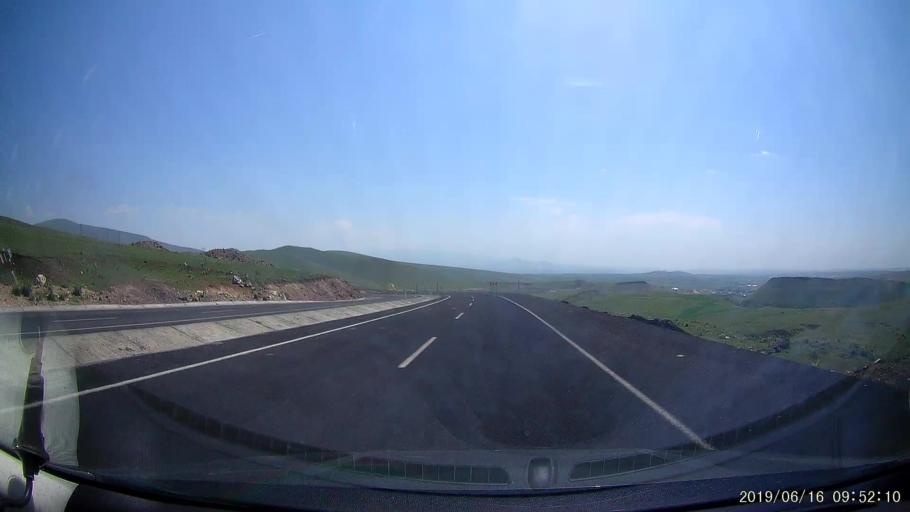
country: TR
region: Kars
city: Digor
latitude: 40.3923
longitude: 43.3813
